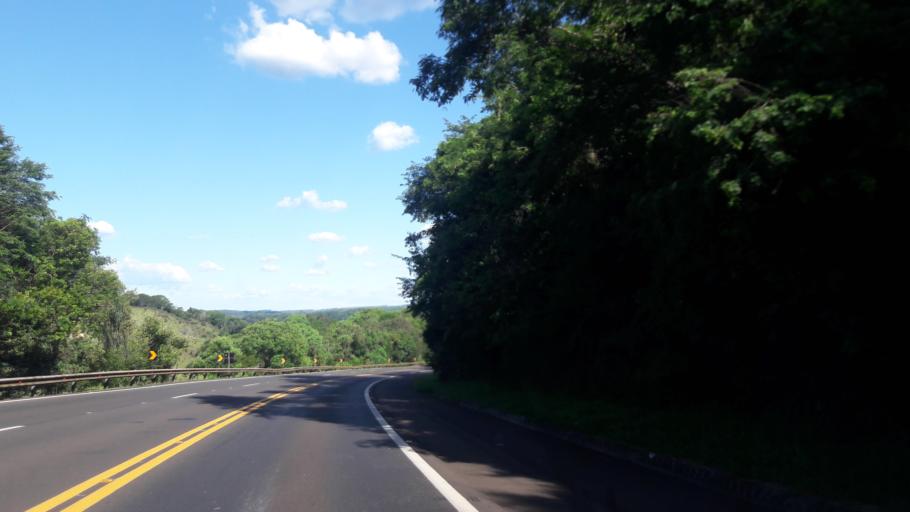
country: BR
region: Parana
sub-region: Laranjeiras Do Sul
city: Laranjeiras do Sul
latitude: -25.4052
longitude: -52.0934
